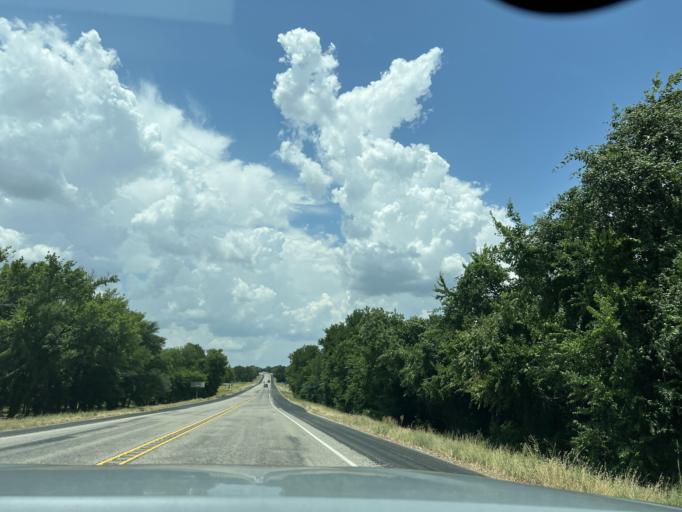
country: US
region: Texas
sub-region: Palo Pinto County
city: Palo Pinto
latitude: 32.7681
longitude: -98.3054
